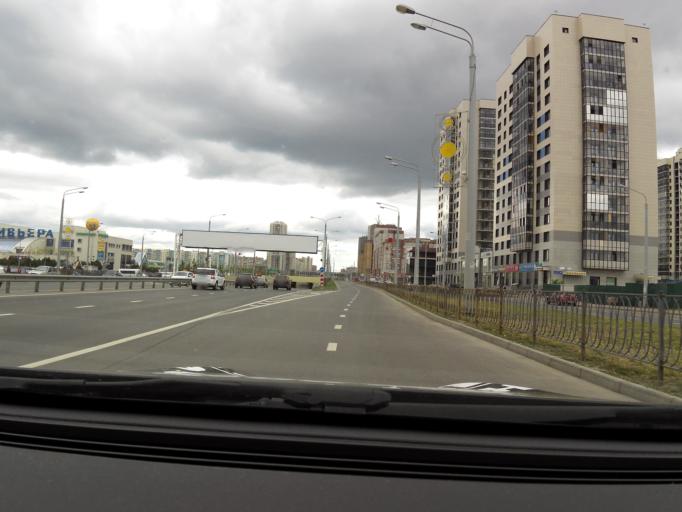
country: RU
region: Tatarstan
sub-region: Gorod Kazan'
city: Kazan
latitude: 55.8135
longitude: 49.1339
